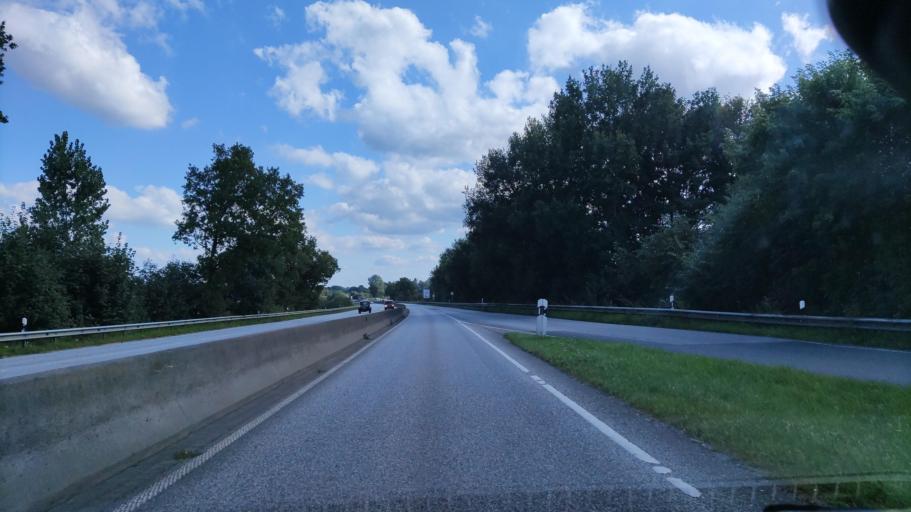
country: DE
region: Schleswig-Holstein
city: Fockbek
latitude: 54.3086
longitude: 9.6290
